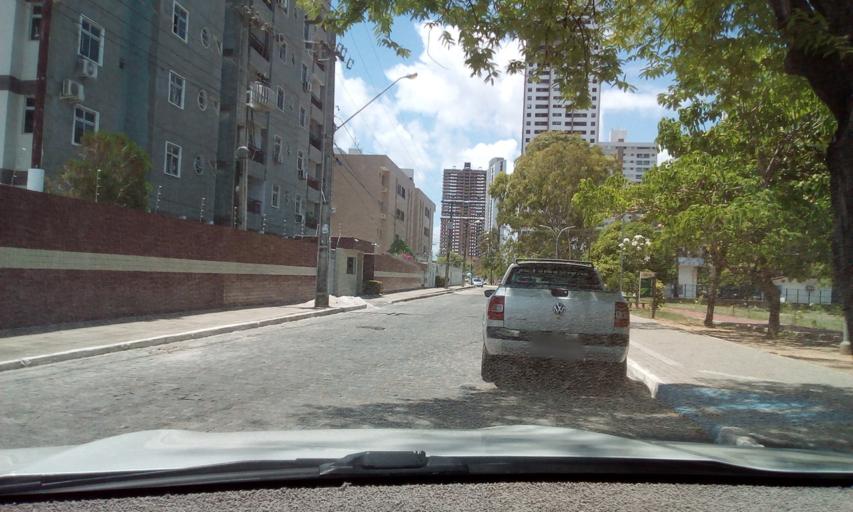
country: BR
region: Paraiba
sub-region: Joao Pessoa
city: Joao Pessoa
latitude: -7.0844
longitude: -34.8350
